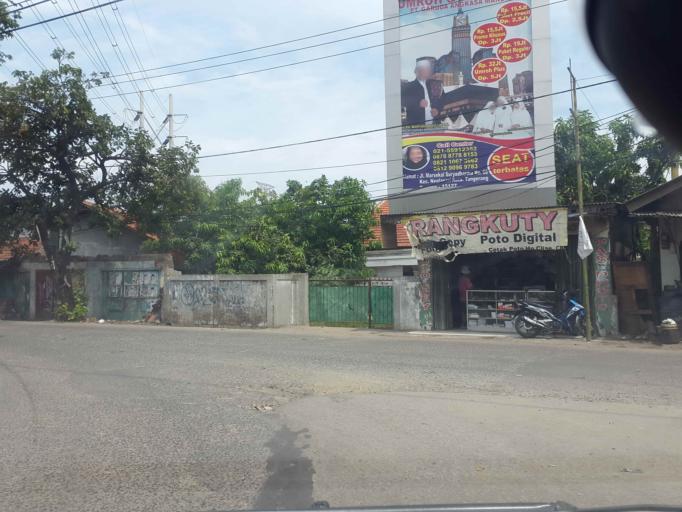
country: ID
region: Banten
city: Tangerang
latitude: -6.1538
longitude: 106.6567
